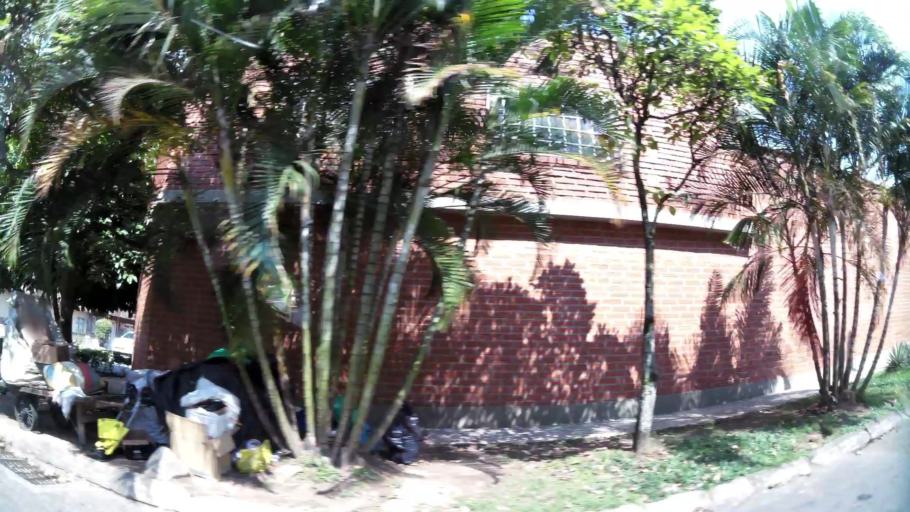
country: CO
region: Antioquia
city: Medellin
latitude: 6.2295
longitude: -75.5945
